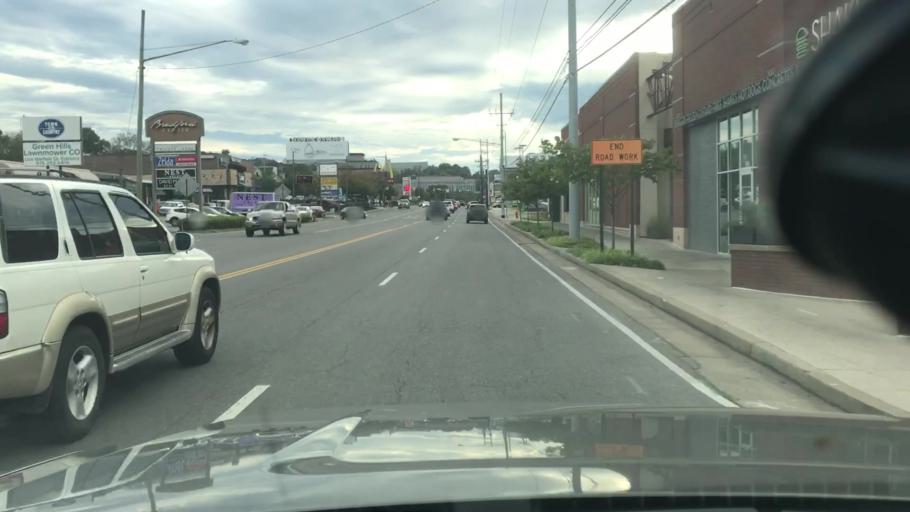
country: US
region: Tennessee
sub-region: Davidson County
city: Oak Hill
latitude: 36.1032
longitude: -86.8164
